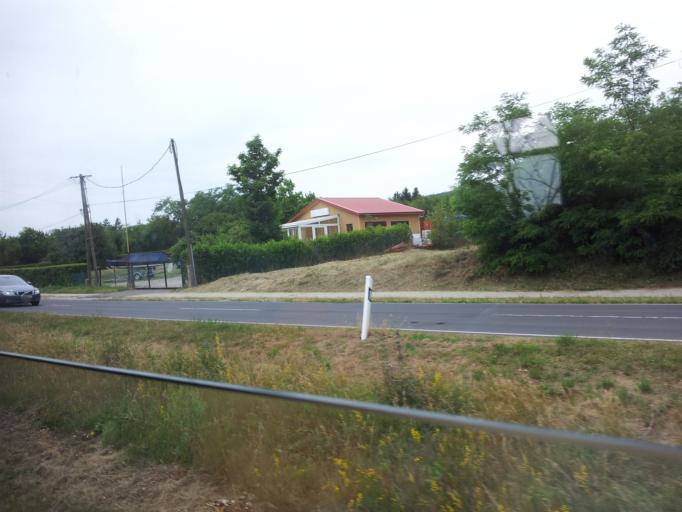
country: HU
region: Veszprem
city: Revfueloep
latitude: 46.8423
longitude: 17.6520
